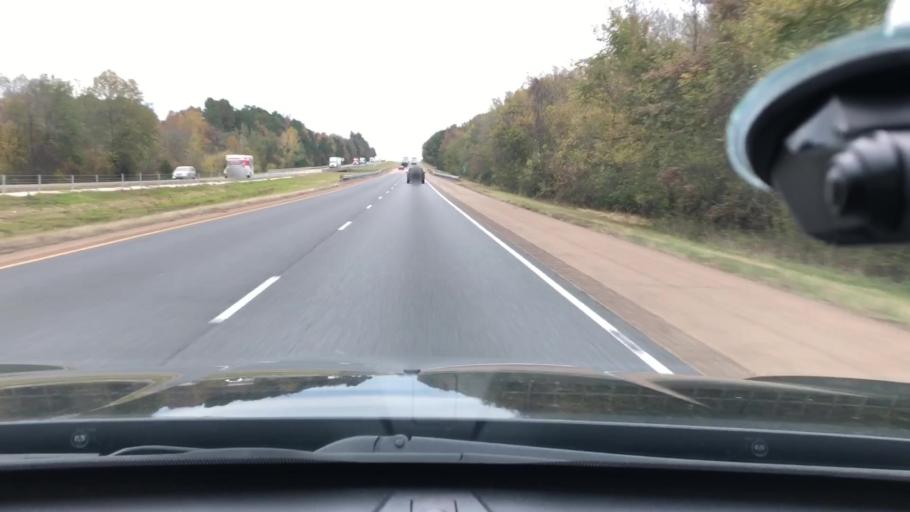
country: US
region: Arkansas
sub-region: Clark County
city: Gurdon
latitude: 33.9858
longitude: -93.1946
